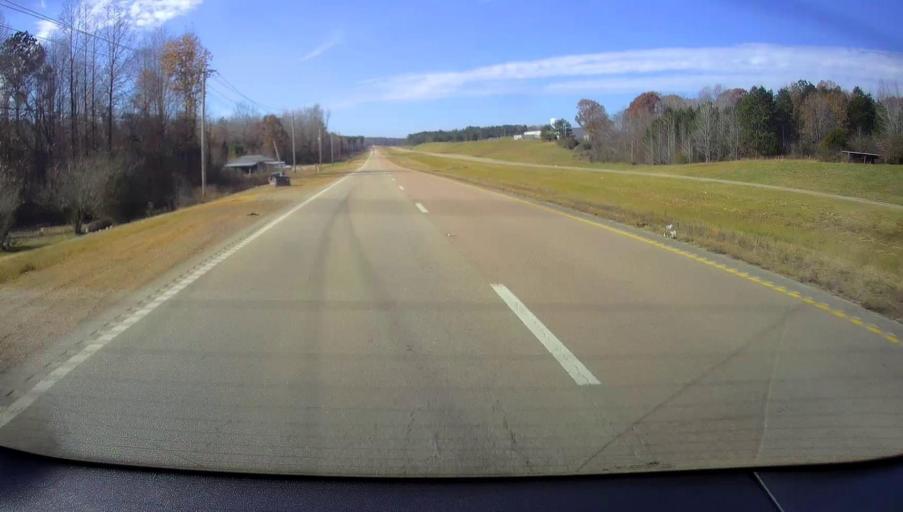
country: US
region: Mississippi
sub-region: Tippah County
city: Ripley
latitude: 34.9504
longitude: -88.9262
